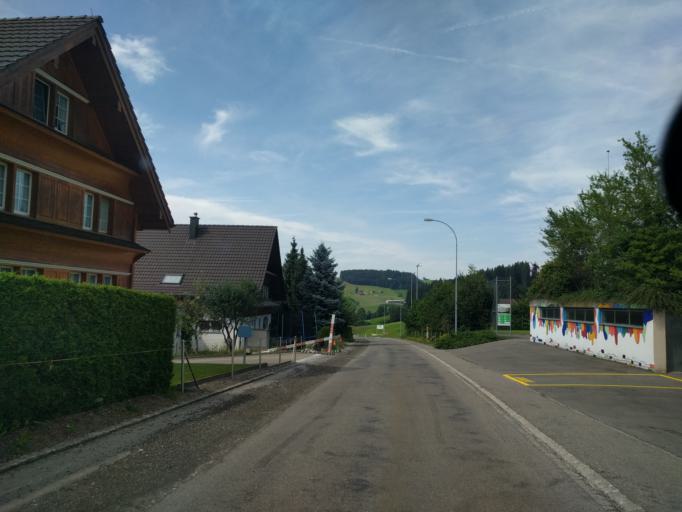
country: CH
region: Saint Gallen
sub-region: Wahlkreis Toggenburg
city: Sankt Peterzell
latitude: 47.3068
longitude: 9.1954
